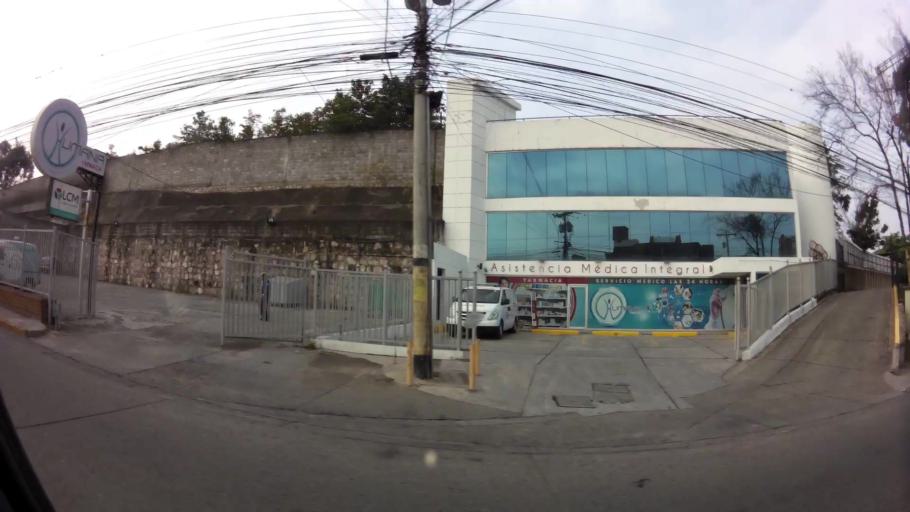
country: HN
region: Francisco Morazan
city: Tegucigalpa
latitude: 14.0847
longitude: -87.1834
